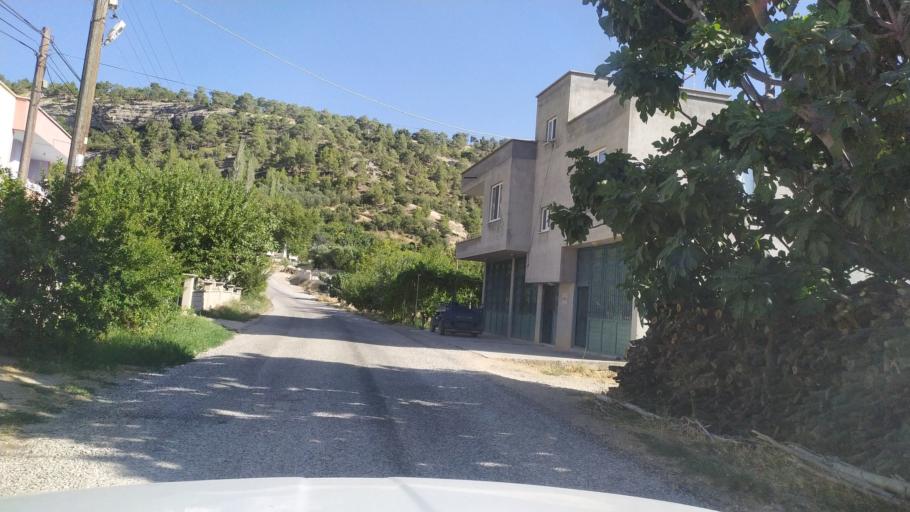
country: TR
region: Mersin
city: Mut
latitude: 36.7066
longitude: 33.4732
